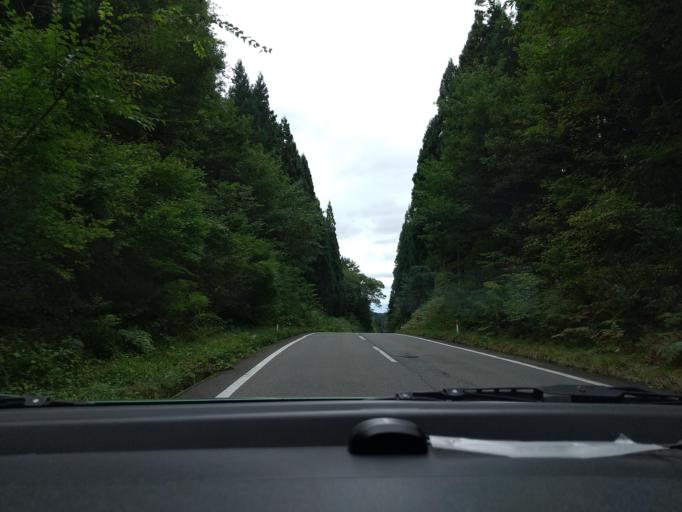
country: JP
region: Akita
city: Kakunodatemachi
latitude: 39.5675
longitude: 140.6368
